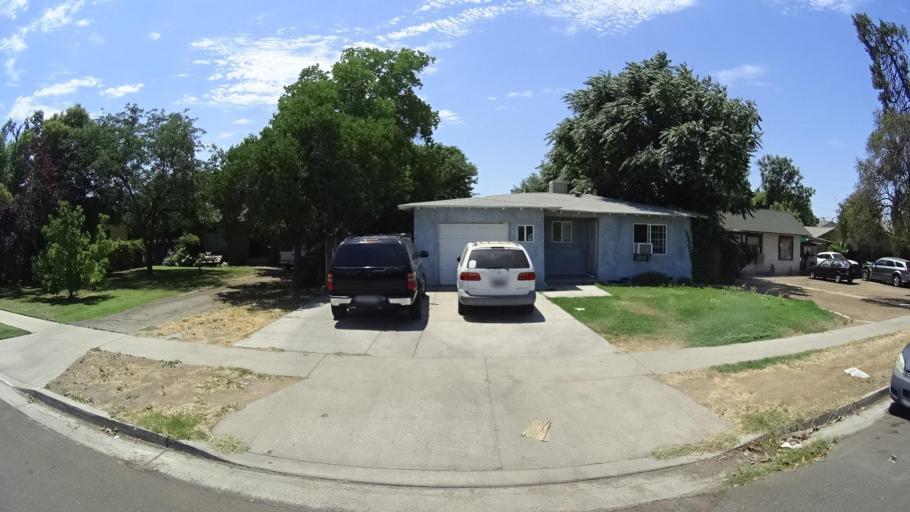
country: US
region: California
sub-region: Fresno County
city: Fresno
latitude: 36.7313
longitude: -119.7443
